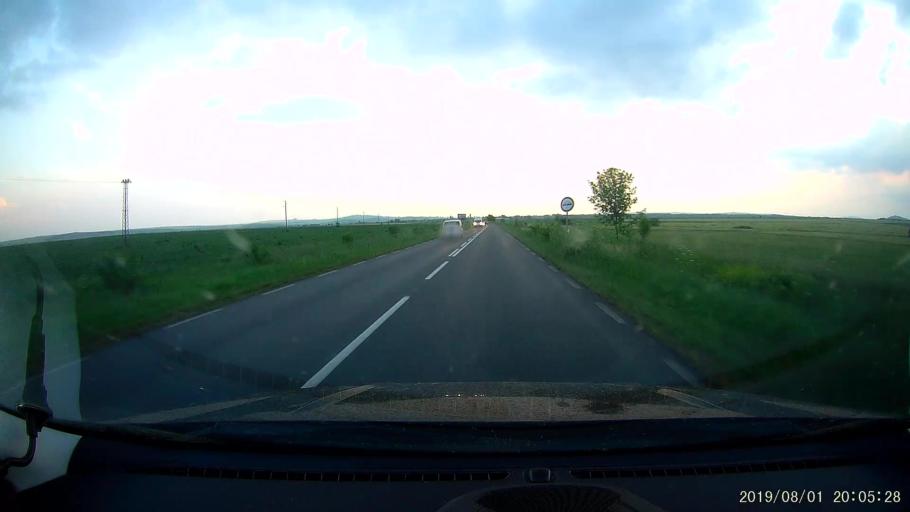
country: BG
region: Yambol
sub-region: Obshtina Yambol
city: Yambol
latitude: 42.5457
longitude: 26.5663
